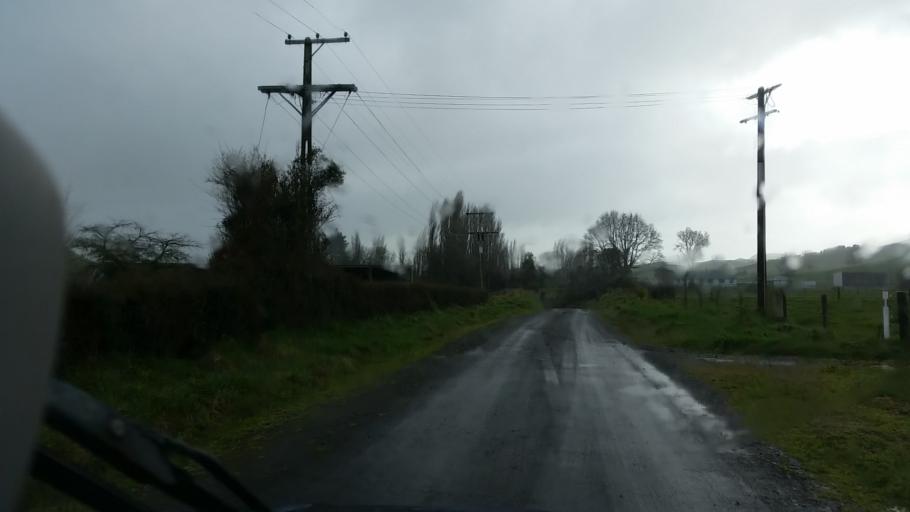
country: NZ
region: Taranaki
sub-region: South Taranaki District
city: Eltham
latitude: -39.3455
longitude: 174.4381
